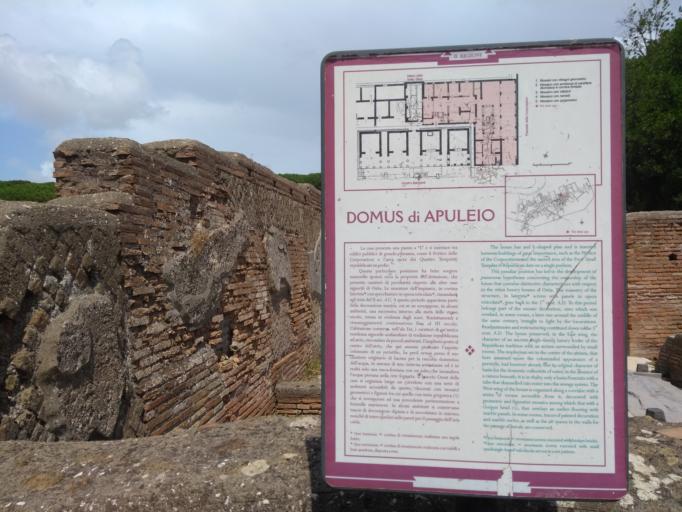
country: IT
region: Latium
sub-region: Citta metropolitana di Roma Capitale
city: Lido di Ostia
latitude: 41.7557
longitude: 12.2909
